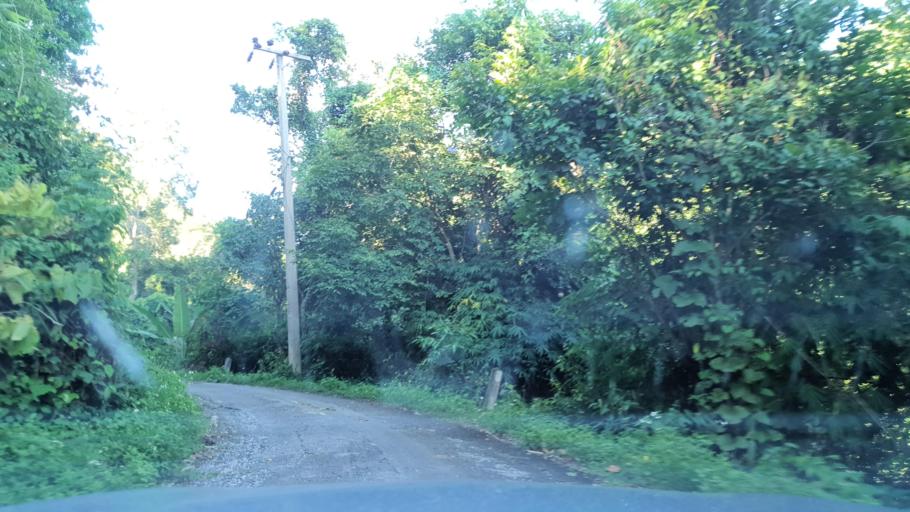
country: TH
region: Chiang Mai
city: Mae On
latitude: 18.8144
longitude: 99.3348
